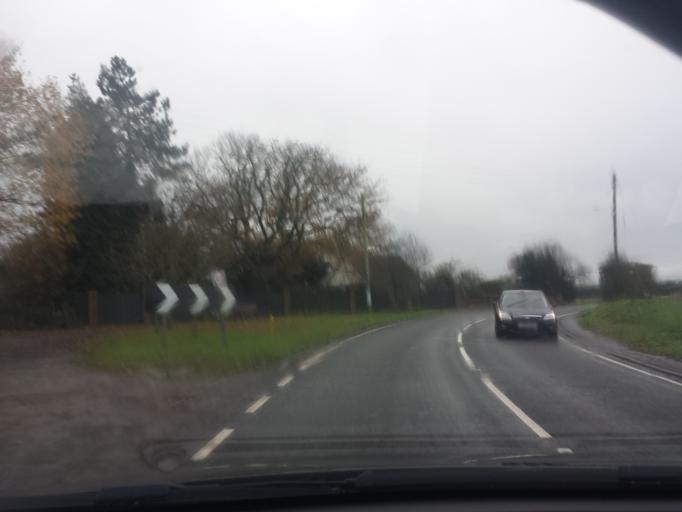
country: GB
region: England
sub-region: Essex
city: Little Clacton
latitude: 51.8436
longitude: 1.1605
